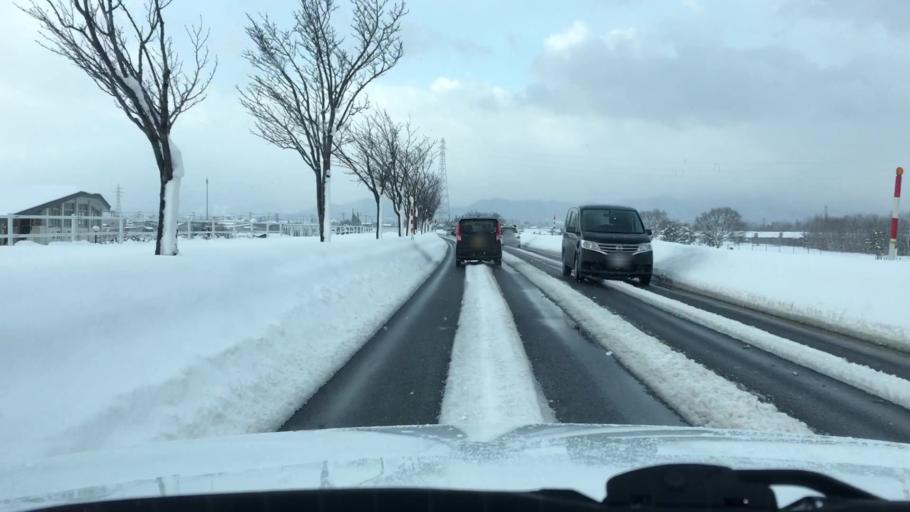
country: JP
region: Aomori
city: Hirosaki
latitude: 40.6323
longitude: 140.4729
